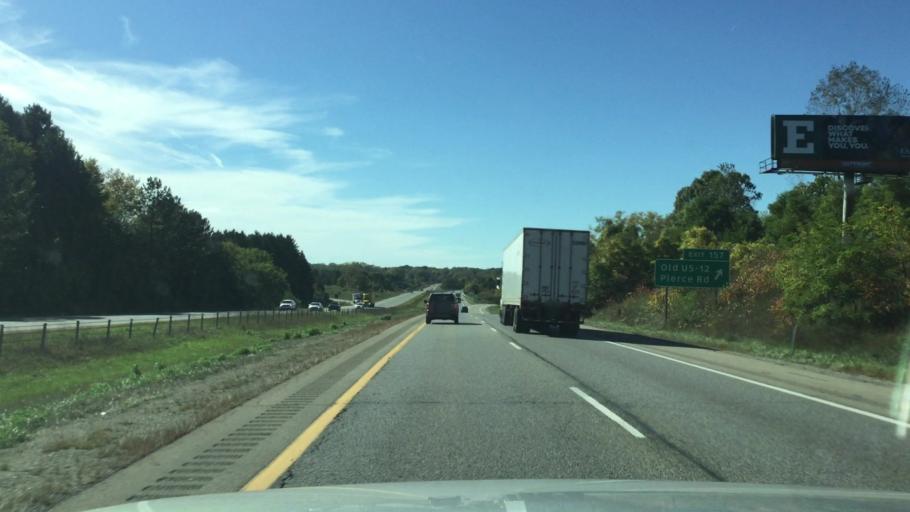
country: US
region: Michigan
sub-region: Washtenaw County
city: Chelsea
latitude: 42.2931
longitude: -84.0607
